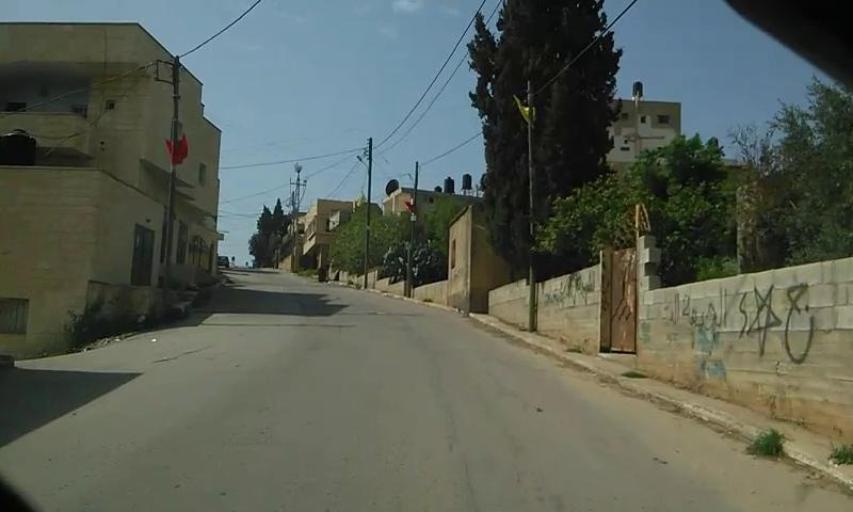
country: PS
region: West Bank
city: `Anin
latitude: 32.5014
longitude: 35.1707
